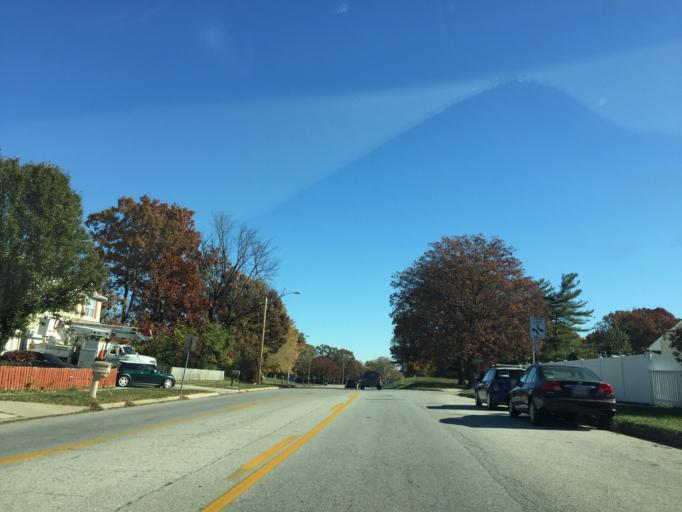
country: US
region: Maryland
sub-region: Baltimore County
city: Lansdowne
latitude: 39.2515
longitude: -76.6587
